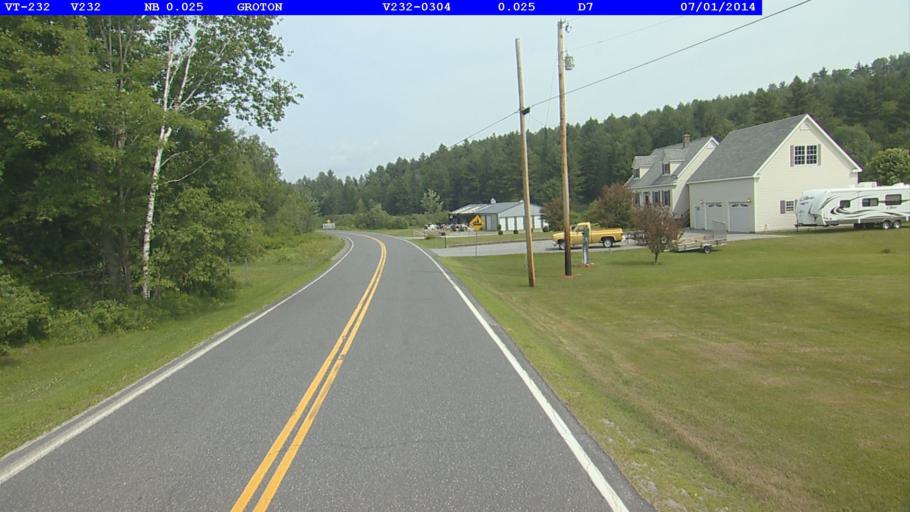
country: US
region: New Hampshire
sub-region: Grafton County
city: Woodsville
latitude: 44.2200
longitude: -72.2257
